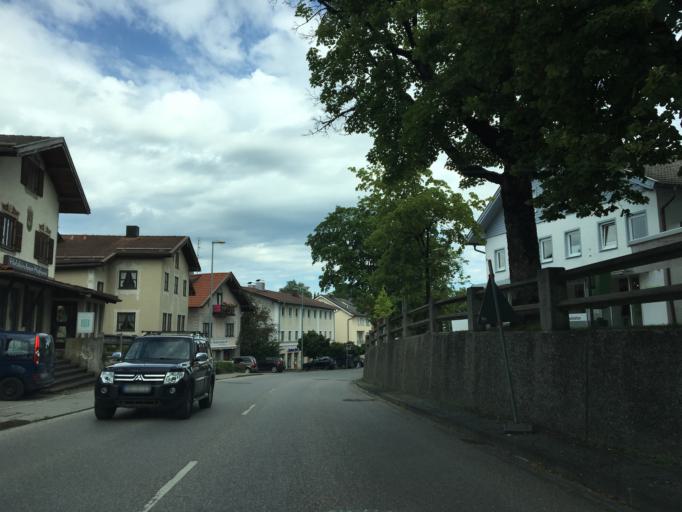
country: DE
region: Bavaria
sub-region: Upper Bavaria
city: Holzkirchen
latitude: 47.8804
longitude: 11.6989
